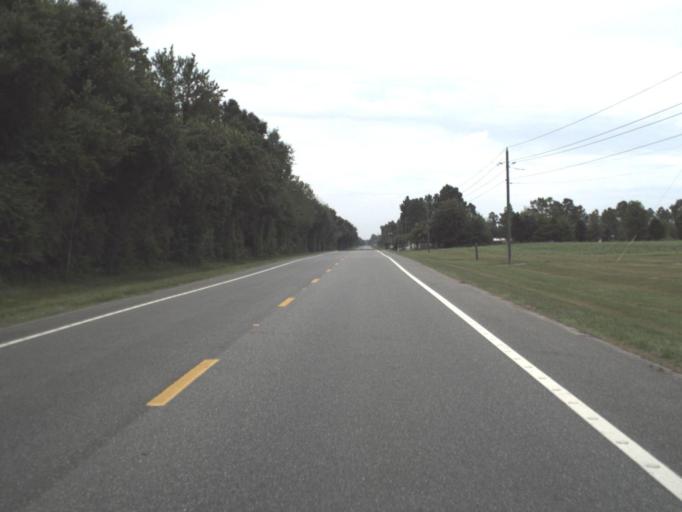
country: US
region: Florida
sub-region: Suwannee County
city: Wellborn
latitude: 30.1056
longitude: -82.9480
